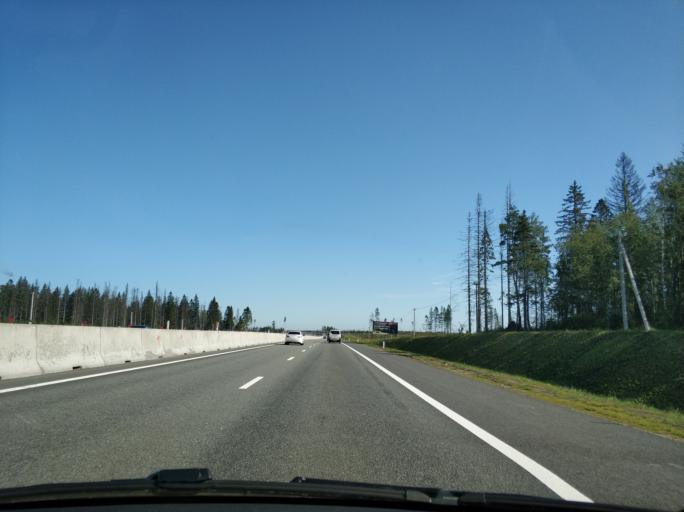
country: RU
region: Leningrad
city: Sosnovo
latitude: 60.4913
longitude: 30.1959
